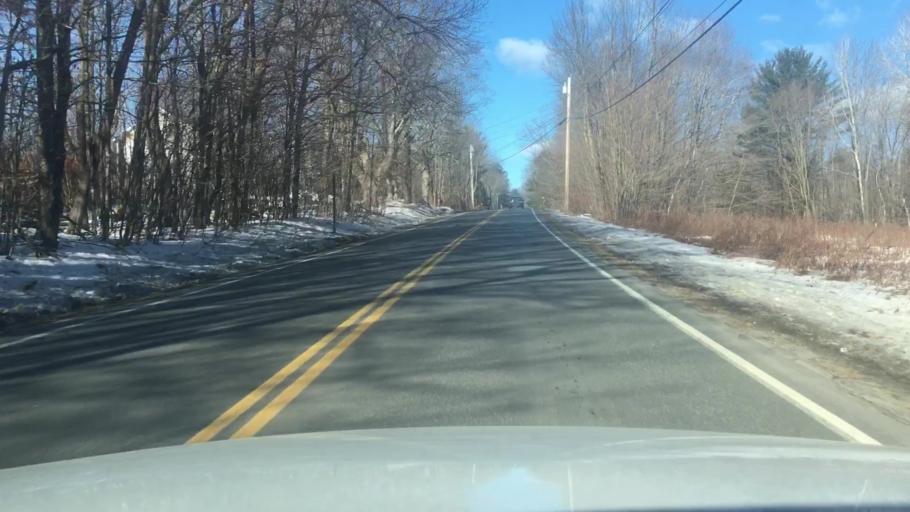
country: US
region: Maine
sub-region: Somerset County
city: Skowhegan
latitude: 44.7275
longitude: -69.6771
